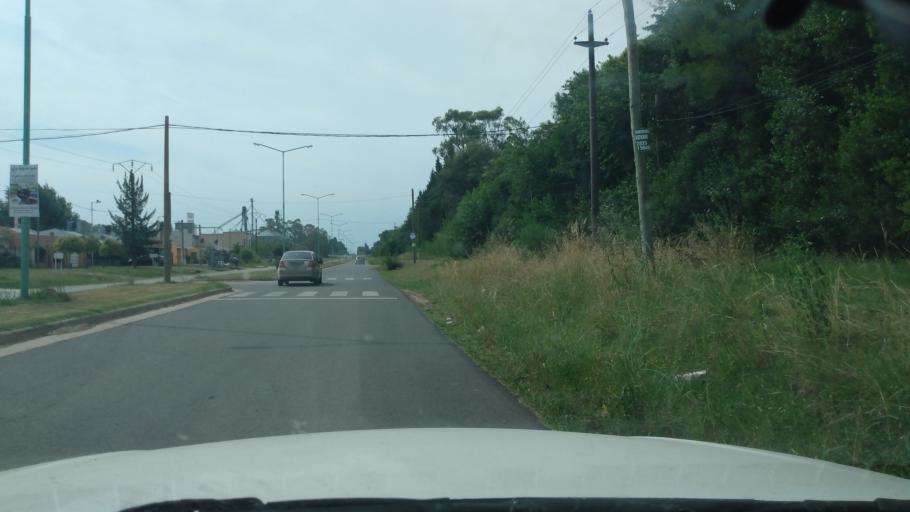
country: AR
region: Buenos Aires
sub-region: Partido de Lujan
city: Lujan
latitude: -34.5539
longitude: -59.1328
